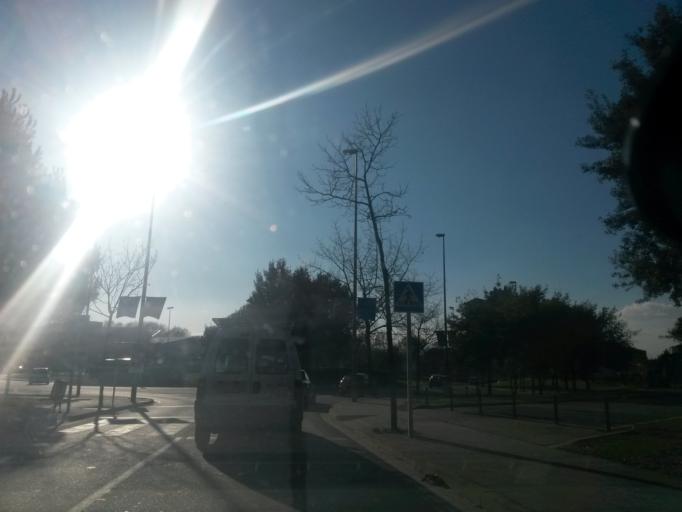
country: ES
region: Catalonia
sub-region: Provincia de Girona
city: Girona
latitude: 41.9928
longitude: 2.8122
